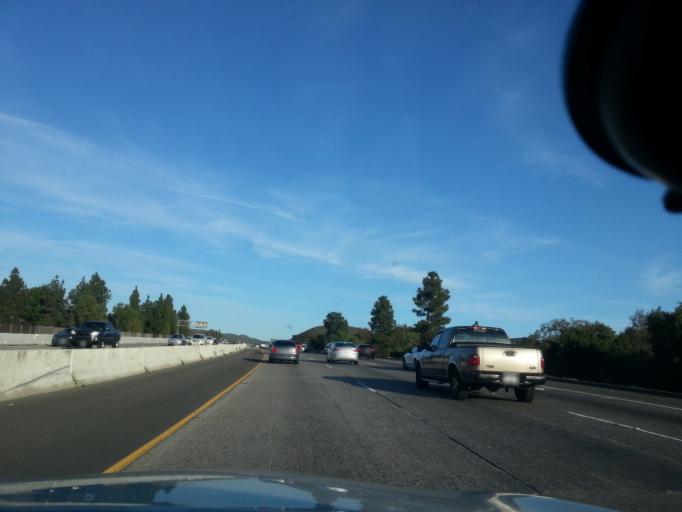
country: US
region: California
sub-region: Ventura County
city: Thousand Oaks
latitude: 34.1775
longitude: -118.8781
